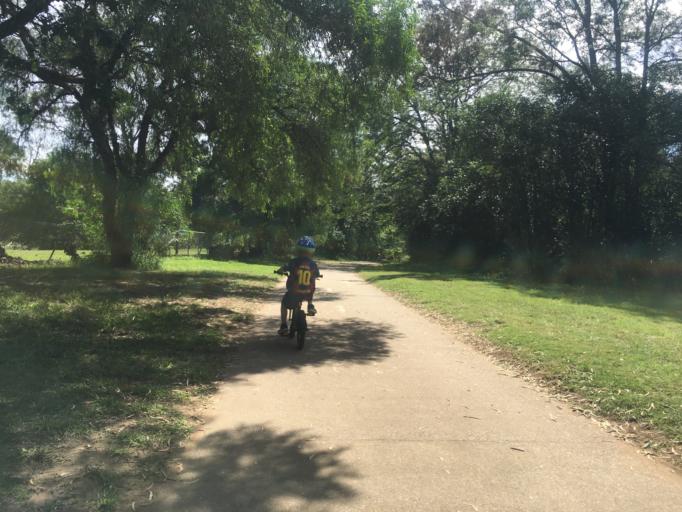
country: AU
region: New South Wales
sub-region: Camden
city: Camden South
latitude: -34.0741
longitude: 150.7002
